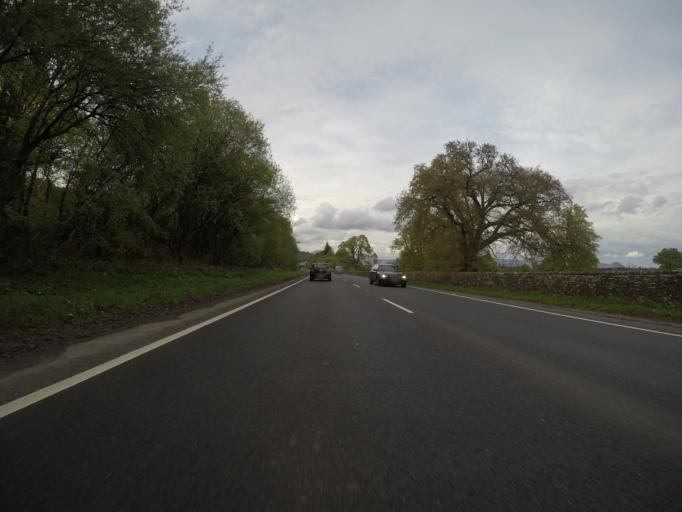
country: GB
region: Scotland
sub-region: West Dunbartonshire
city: Balloch
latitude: 56.0548
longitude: -4.6461
